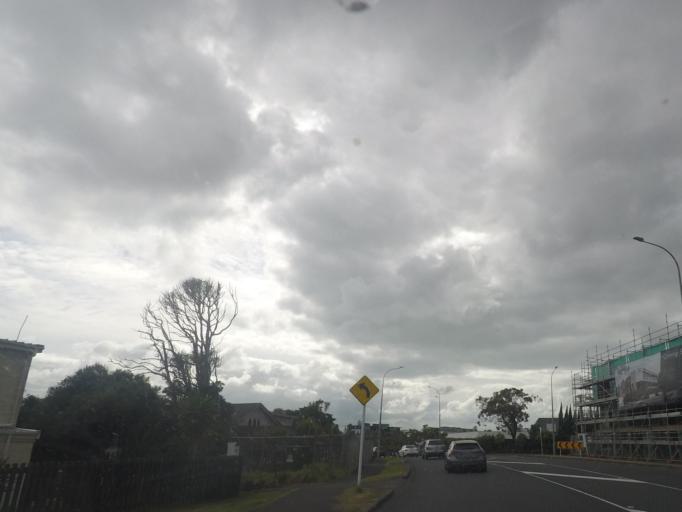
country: NZ
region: Auckland
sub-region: Auckland
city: Tamaki
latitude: -36.8612
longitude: 174.8262
